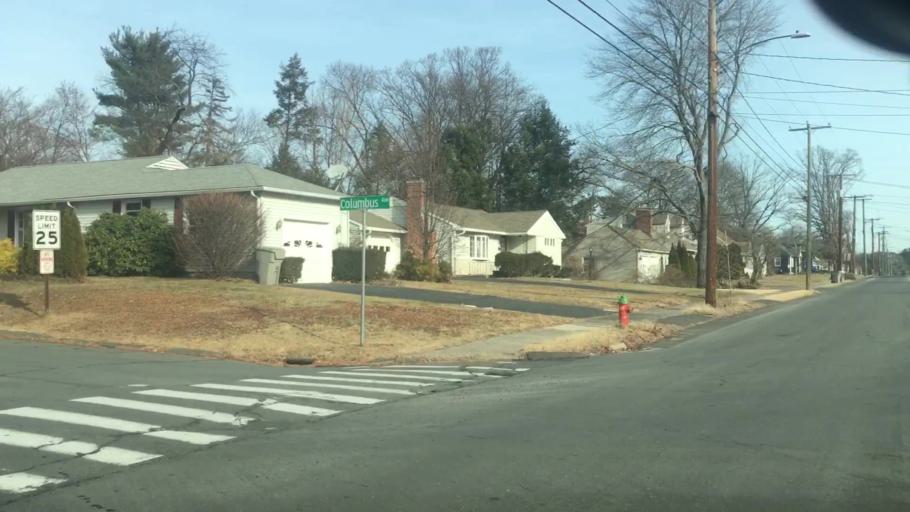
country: US
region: Connecticut
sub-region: Hartford County
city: Bristol
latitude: 41.6886
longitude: -72.9223
